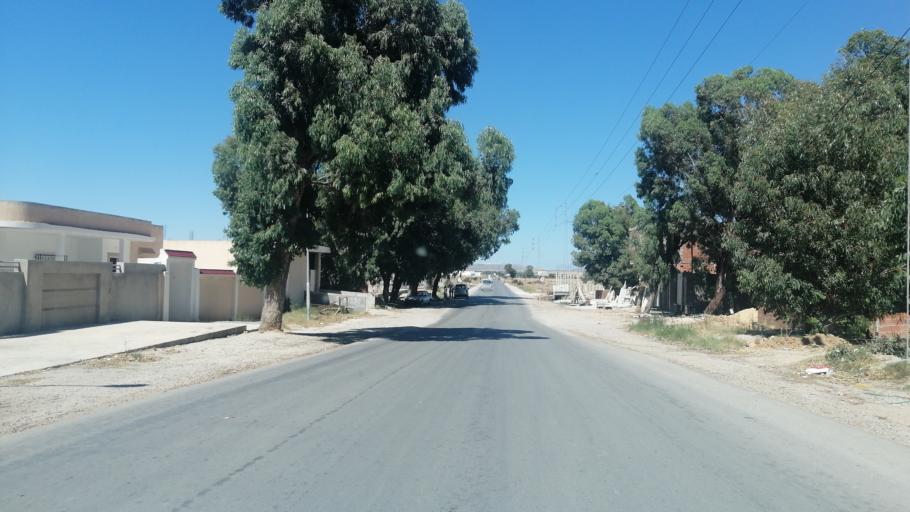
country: TN
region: Al Qayrawan
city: Sbikha
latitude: 36.1255
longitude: 10.0962
